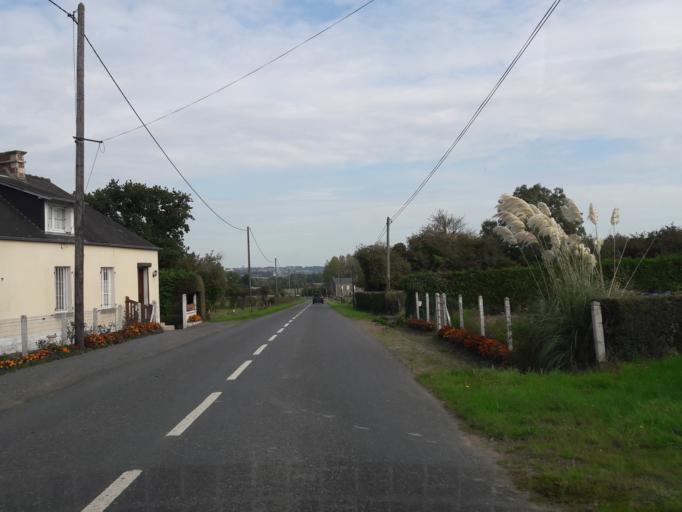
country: FR
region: Lower Normandy
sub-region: Departement du Calvados
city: Saint-Martin-des-Besaces
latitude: 49.0399
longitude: -0.8269
